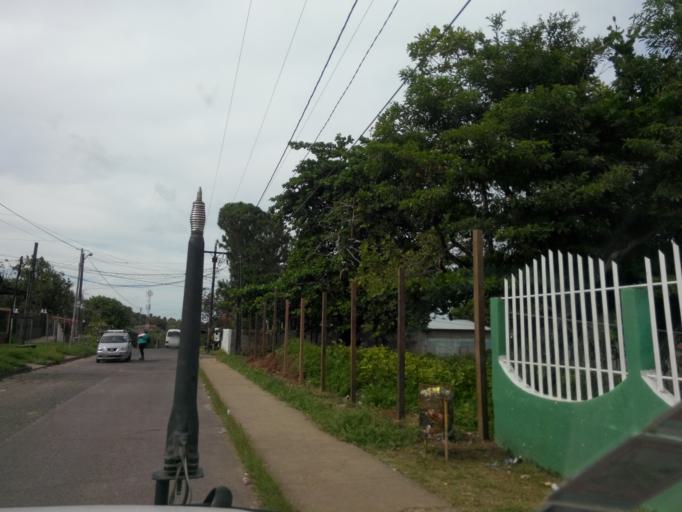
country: NI
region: Atlantico Sur
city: Bluefields
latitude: 12.0176
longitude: -83.7635
